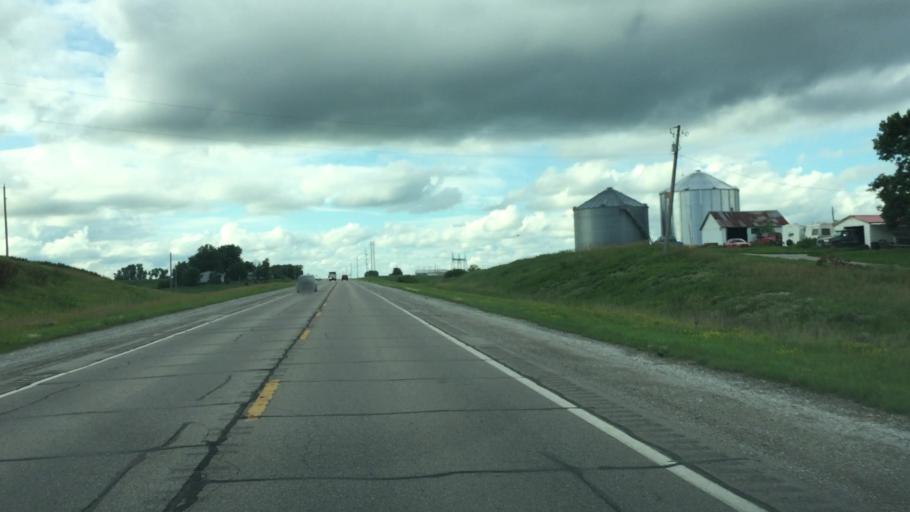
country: US
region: Iowa
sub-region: Jasper County
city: Monroe
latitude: 41.5665
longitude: -93.0970
